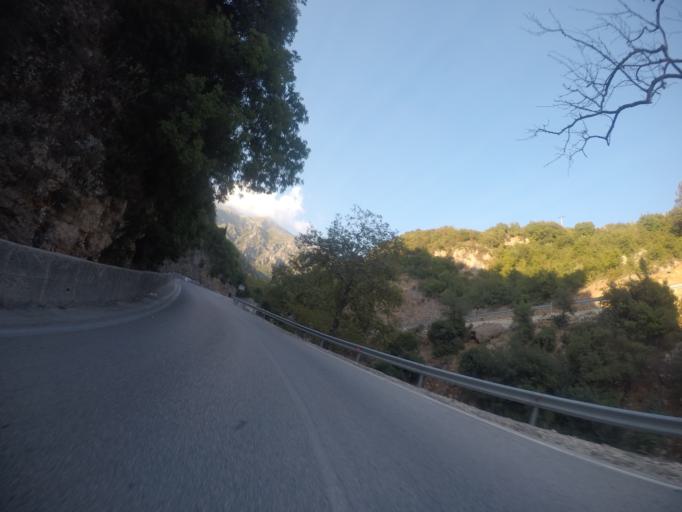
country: AL
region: Vlore
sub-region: Rrethi i Vlores
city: Vranisht
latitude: 40.1432
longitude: 19.6768
